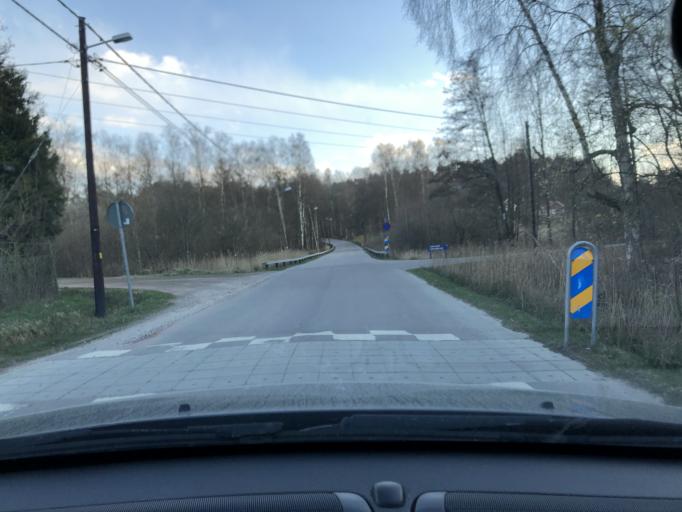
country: SE
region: Vaestra Goetaland
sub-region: Molndal
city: Moelndal
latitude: 57.6964
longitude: 12.0338
